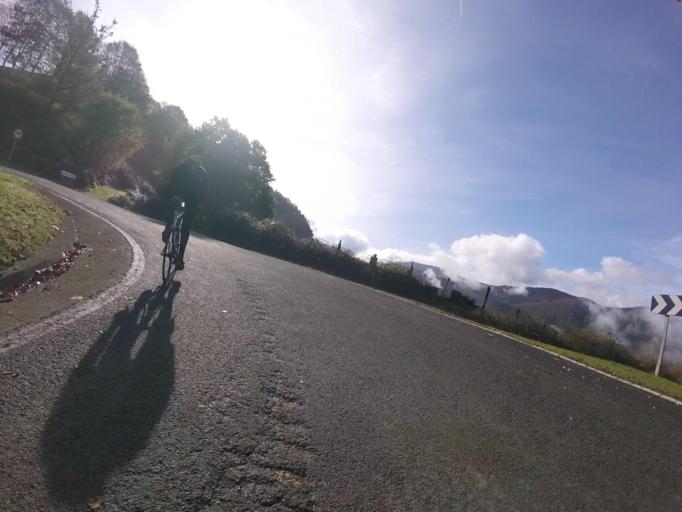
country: ES
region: Navarre
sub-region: Provincia de Navarra
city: Arano
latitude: 43.2042
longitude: -1.8974
